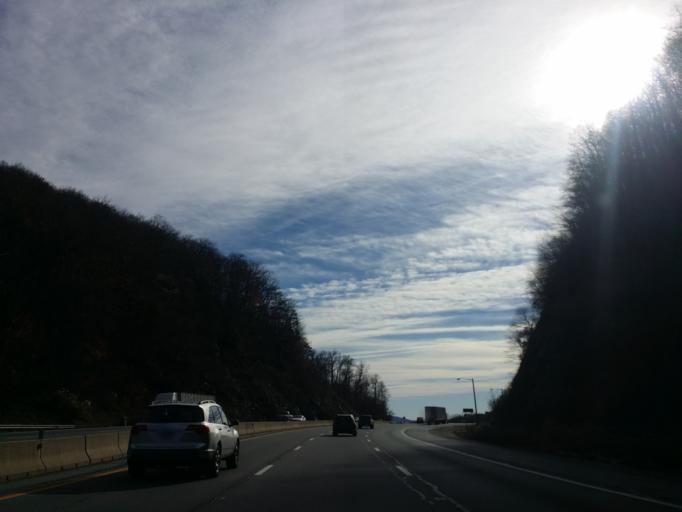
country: US
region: North Carolina
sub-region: Buncombe County
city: Black Mountain
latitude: 35.6190
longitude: -82.2647
